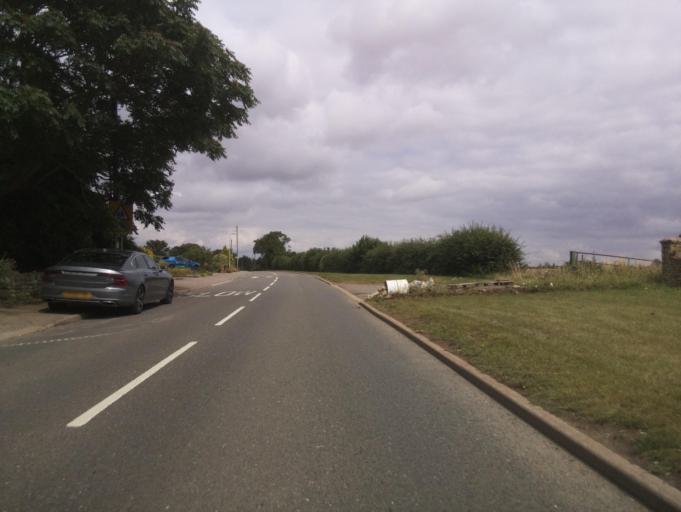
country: GB
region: England
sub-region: District of Rutland
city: Tickencote
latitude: 52.6716
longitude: -0.5201
